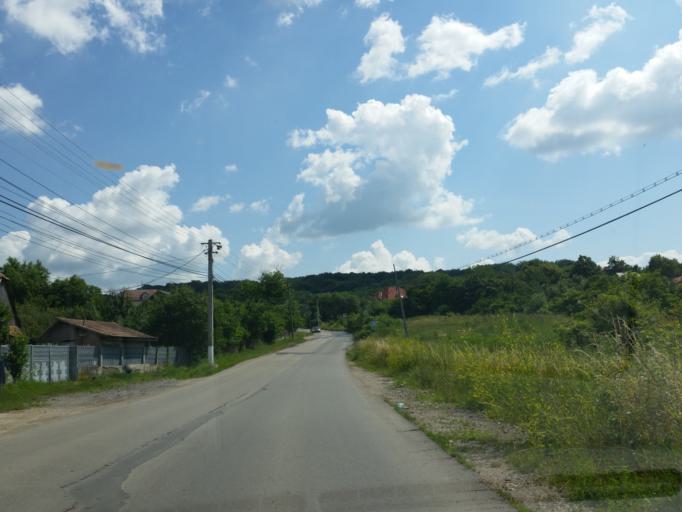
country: RO
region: Cluj
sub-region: Comuna Feleacu
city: Feleacu
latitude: 46.7303
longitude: 23.5871
